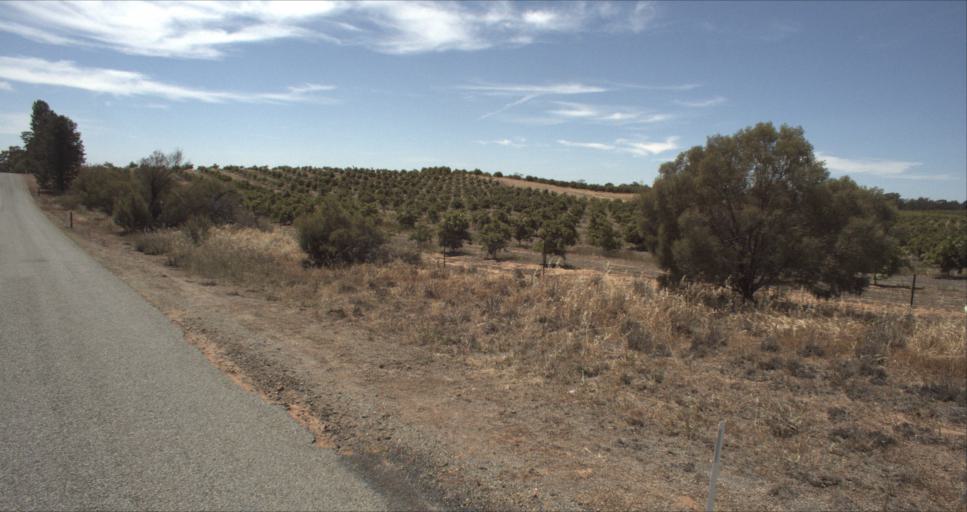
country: AU
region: New South Wales
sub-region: Leeton
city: Leeton
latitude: -34.6689
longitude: 146.4465
